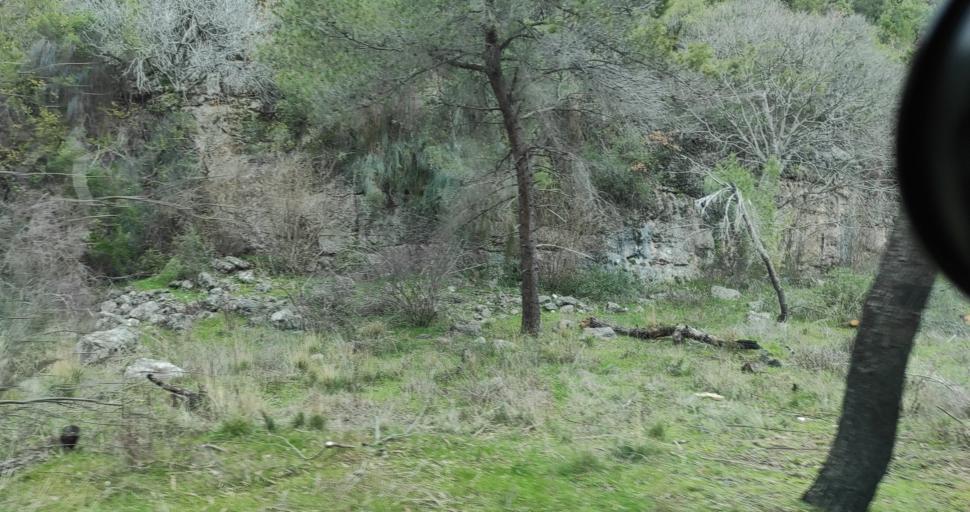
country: AL
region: Lezhe
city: Shengjin
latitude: 41.8239
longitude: 19.5601
